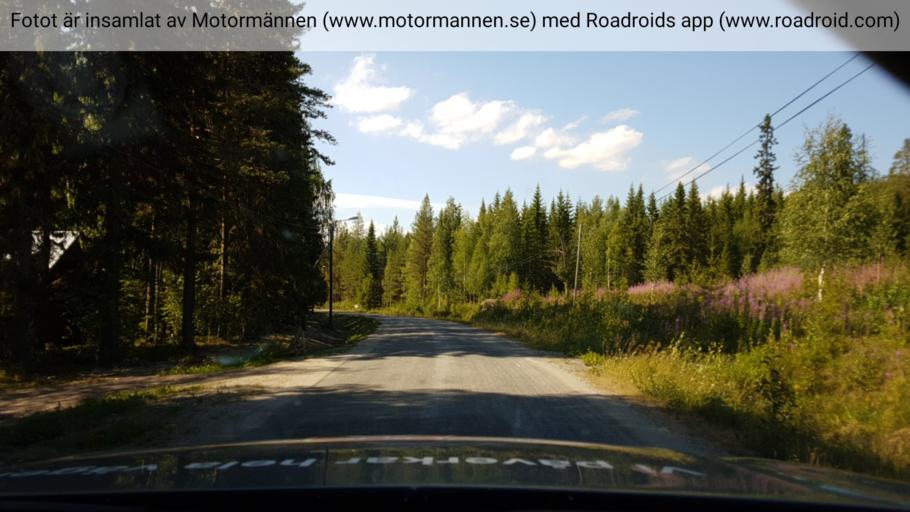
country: SE
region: Vaesterbotten
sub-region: Dorotea Kommun
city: Dorotea
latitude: 64.1051
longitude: 16.3845
